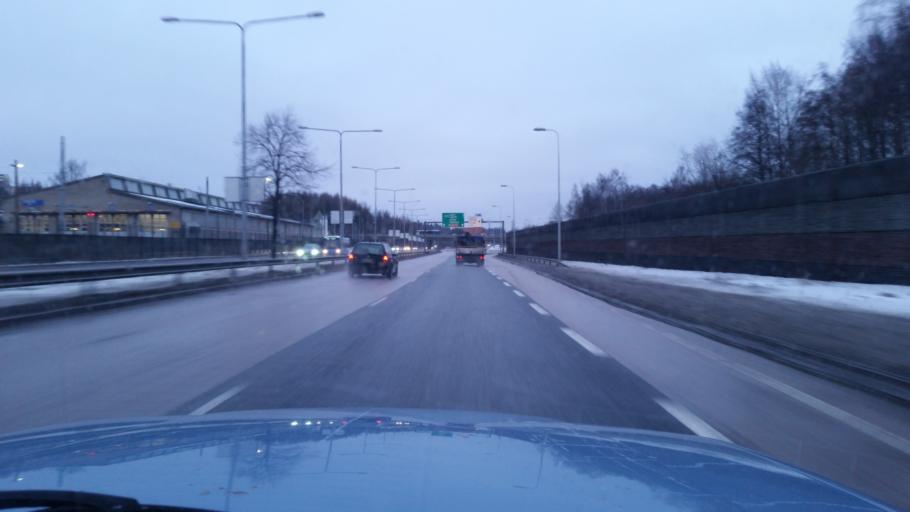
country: FI
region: Uusimaa
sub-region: Helsinki
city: Helsinki
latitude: 60.2136
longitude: 24.9715
